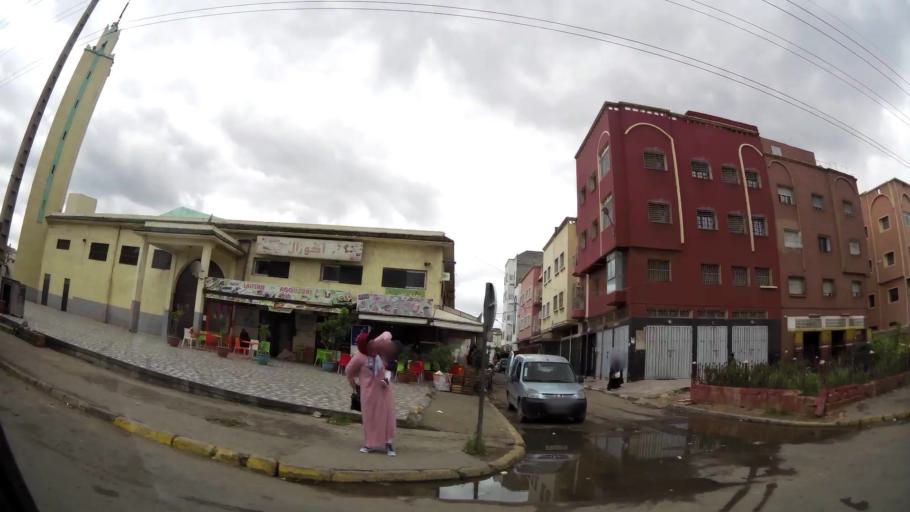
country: MA
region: Grand Casablanca
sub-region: Mediouna
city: Tit Mellil
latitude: 33.5754
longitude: -7.5393
